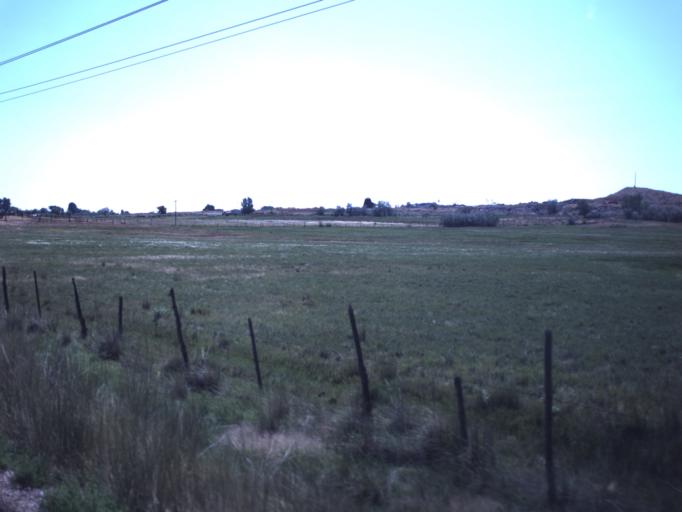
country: US
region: Utah
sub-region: Duchesne County
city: Roosevelt
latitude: 40.4037
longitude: -109.8296
